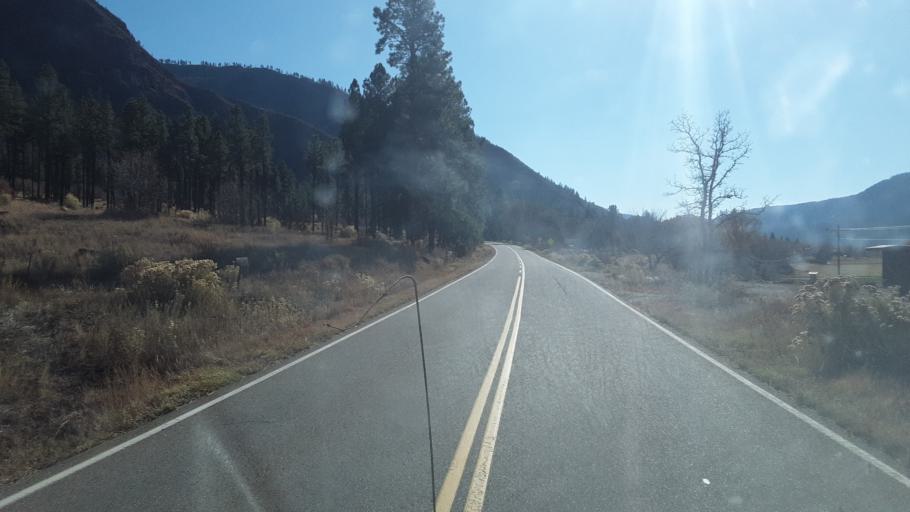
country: US
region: Colorado
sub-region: La Plata County
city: Durango
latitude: 37.4041
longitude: -107.8159
